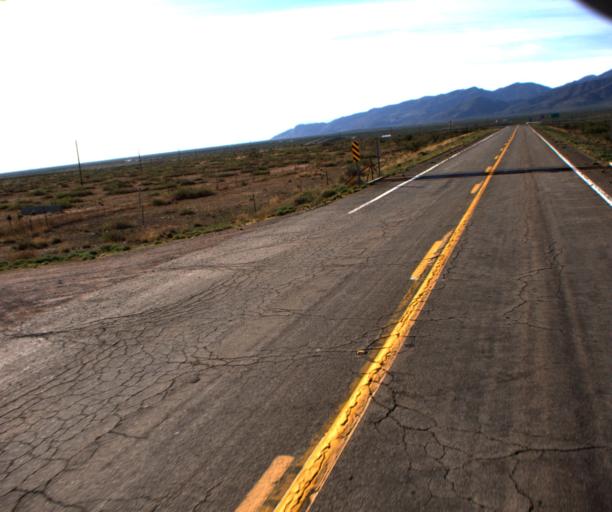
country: US
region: Arizona
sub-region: Cochise County
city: Willcox
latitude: 32.3657
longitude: -109.6228
